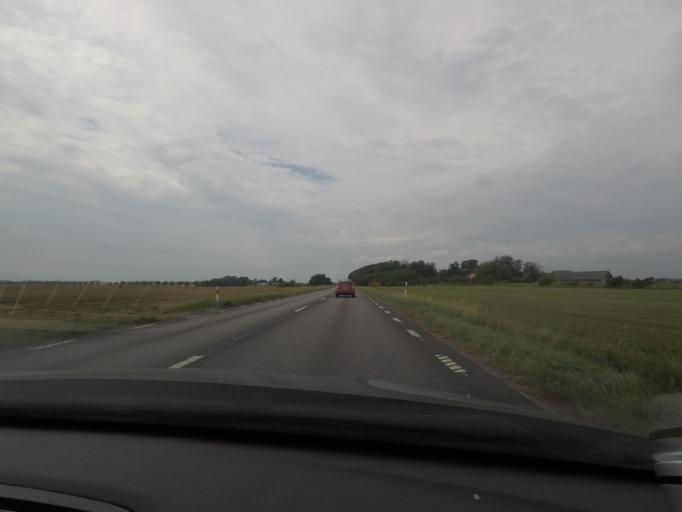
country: SE
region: Halland
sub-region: Halmstads Kommun
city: Paarp
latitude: 56.5994
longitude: 12.9697
